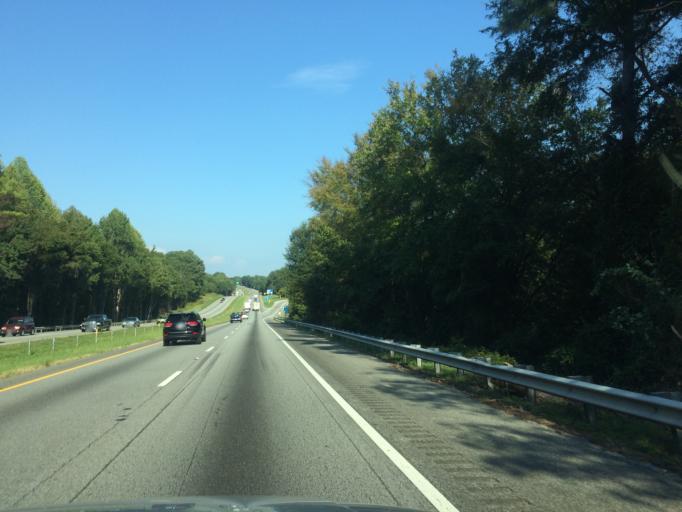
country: US
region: South Carolina
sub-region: Anderson County
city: Centerville
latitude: 34.5653
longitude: -82.7469
